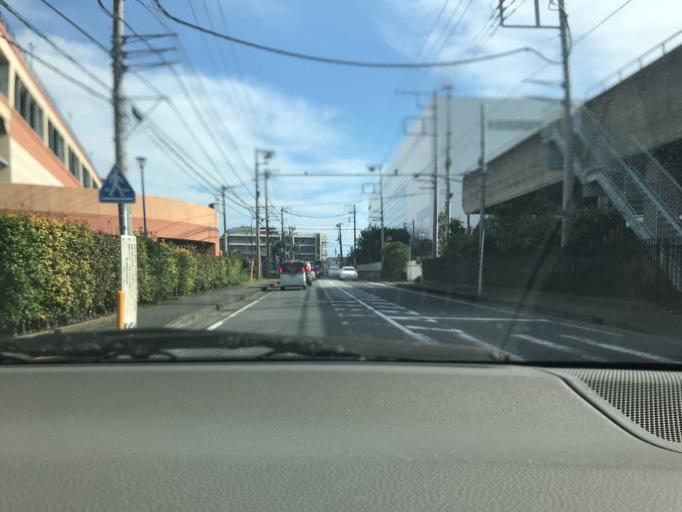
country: JP
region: Kanagawa
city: Fujisawa
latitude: 35.3394
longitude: 139.4630
